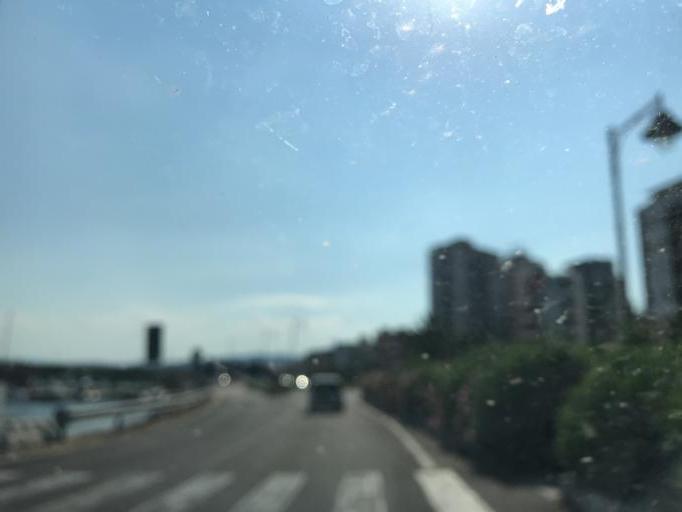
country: IT
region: Sardinia
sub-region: Provincia di Olbia-Tempio
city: Olbia
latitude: 40.9222
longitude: 9.5054
